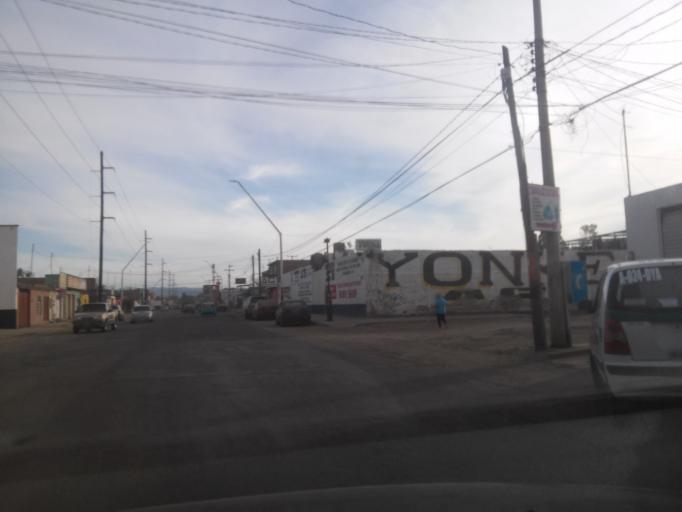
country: MX
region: Durango
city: Victoria de Durango
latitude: 24.0163
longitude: -104.6327
